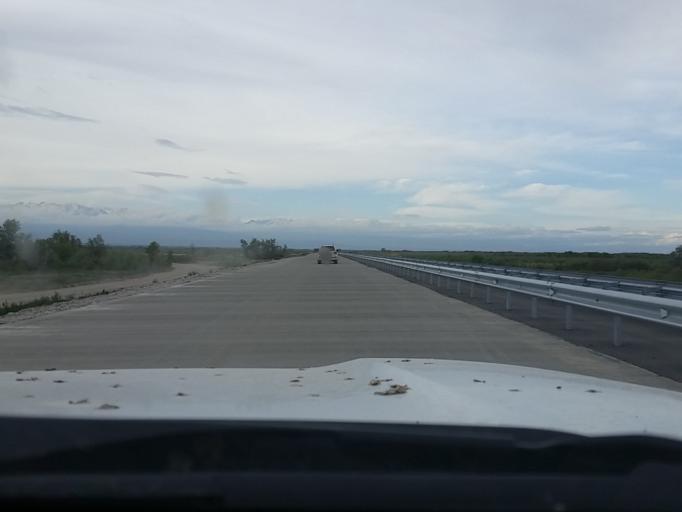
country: KZ
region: Almaty Oblysy
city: Zharkent
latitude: 44.0696
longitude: 80.0334
